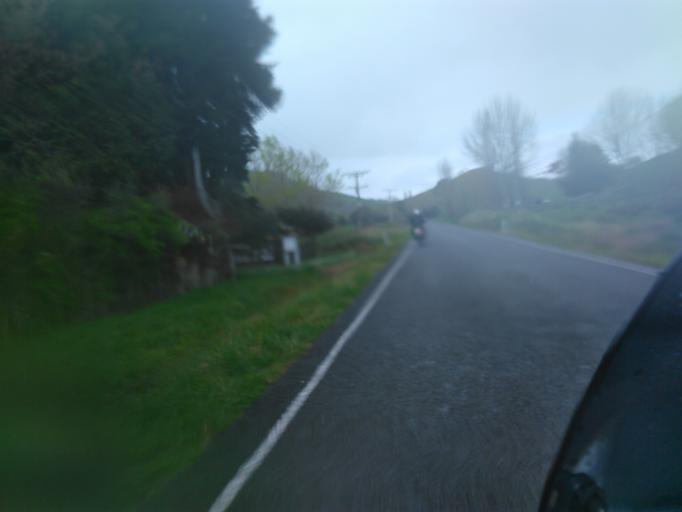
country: NZ
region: Gisborne
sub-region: Gisborne District
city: Gisborne
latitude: -38.6815
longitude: 177.7242
